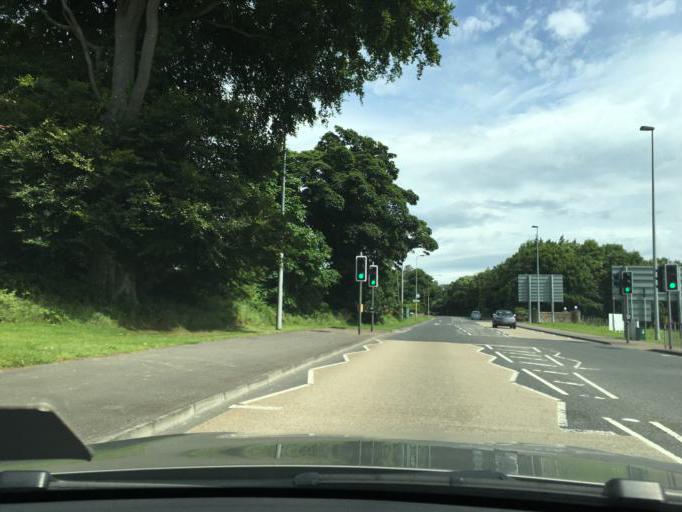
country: GB
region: Northern Ireland
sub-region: City of Derry
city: Derry
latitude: 55.0252
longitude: -7.3019
